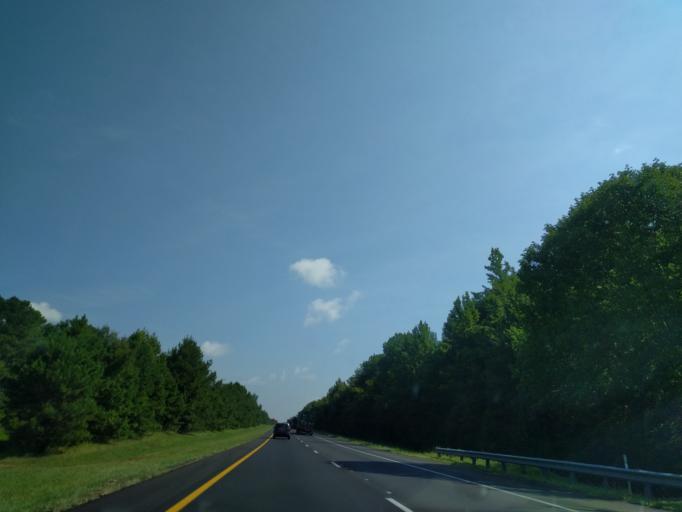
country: US
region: Tennessee
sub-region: Sumner County
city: White House
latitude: 36.4424
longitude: -86.7019
